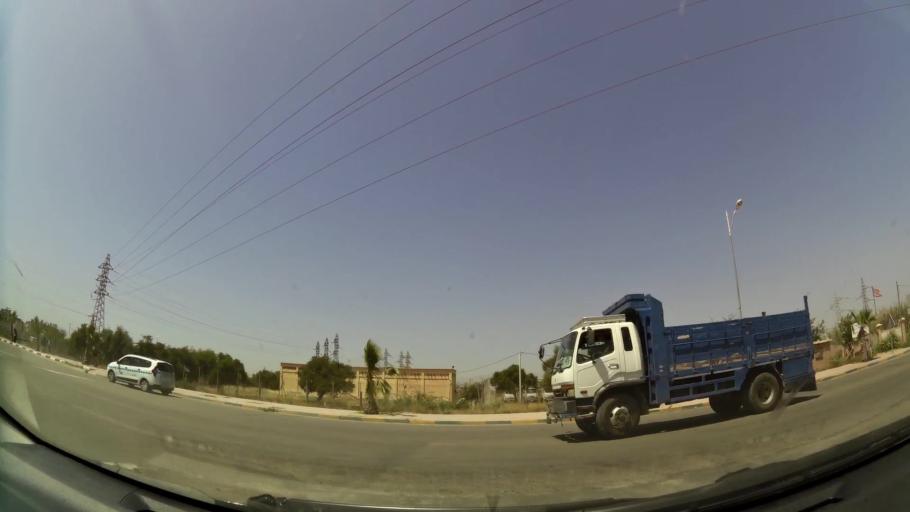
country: MA
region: Souss-Massa-Draa
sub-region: Inezgane-Ait Mellou
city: Inezgane
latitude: 30.3533
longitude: -9.4879
